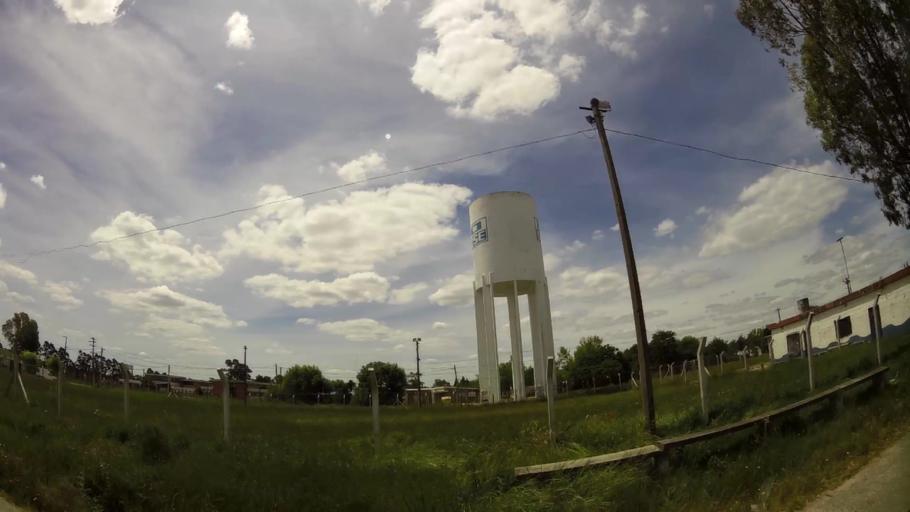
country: UY
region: San Jose
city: Delta del Tigre
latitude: -34.7523
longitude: -56.4202
